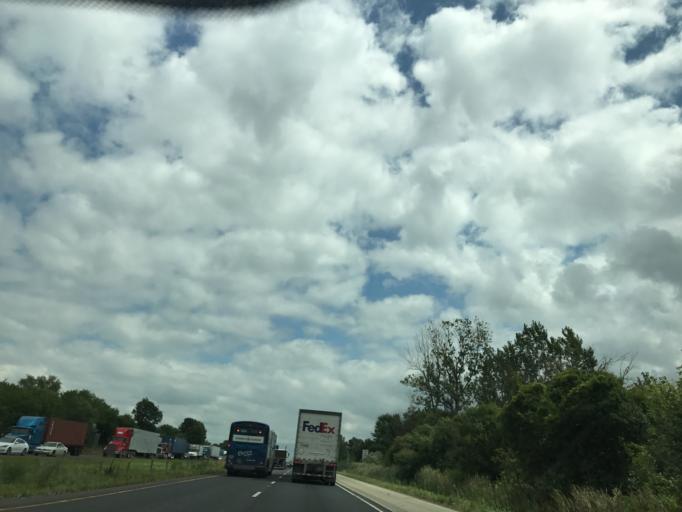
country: US
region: Illinois
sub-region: Will County
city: Ingalls Park
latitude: 41.5132
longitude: -88.0329
